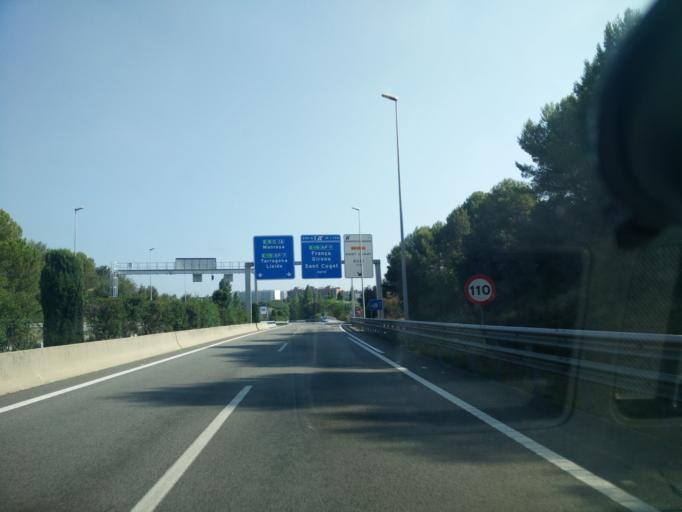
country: ES
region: Catalonia
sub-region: Provincia de Barcelona
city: Sant Cugat del Valles
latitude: 41.4736
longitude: 2.0647
